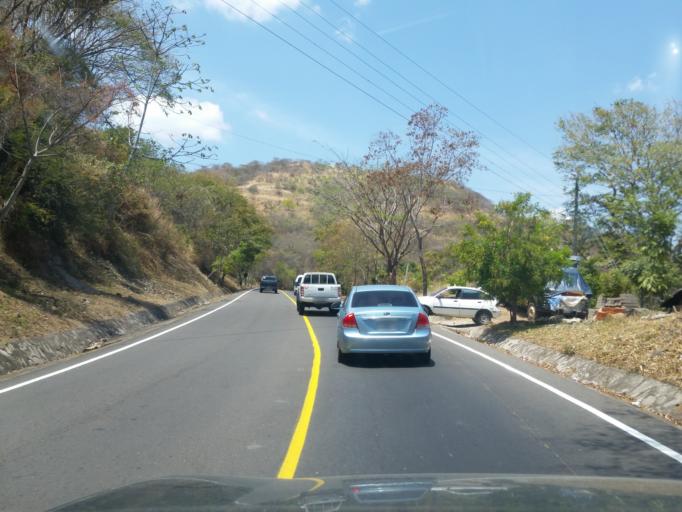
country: NI
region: Esteli
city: Esteli
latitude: 12.9956
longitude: -86.2808
